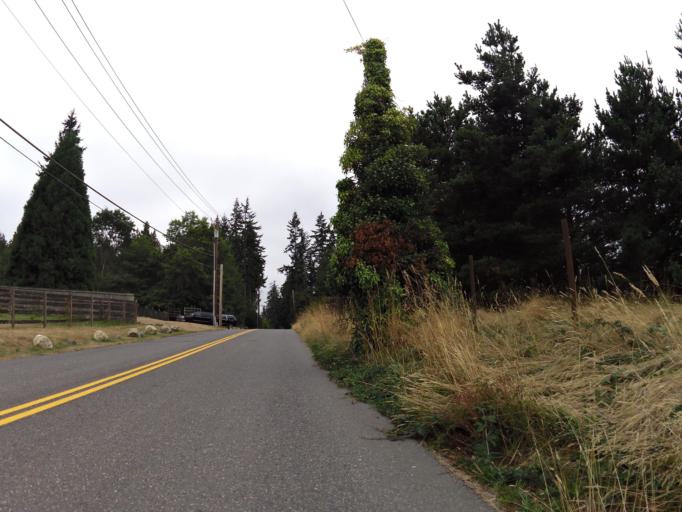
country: US
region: Washington
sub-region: Kitsap County
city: Lofall
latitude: 47.8086
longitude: -122.6600
